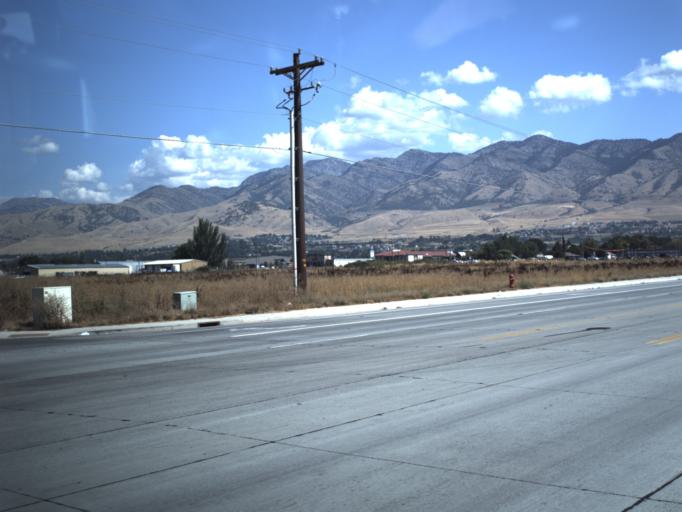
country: US
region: Utah
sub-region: Cache County
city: Hyde Park
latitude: 41.7777
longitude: -111.8388
